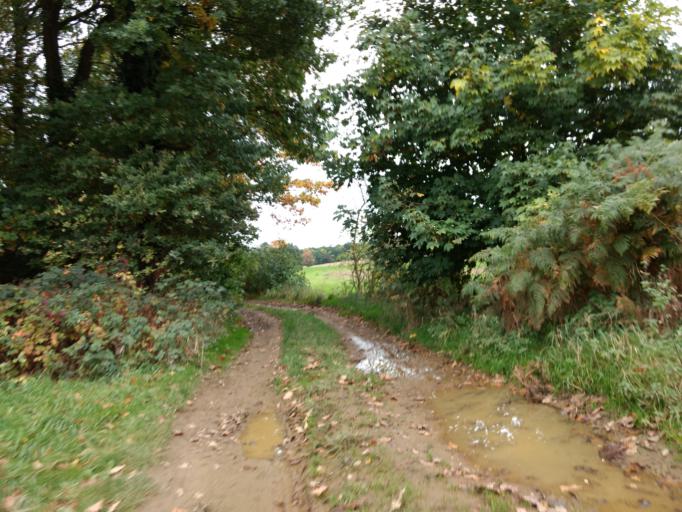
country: BE
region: Flanders
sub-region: Provincie Vlaams-Brabant
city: Diest
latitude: 50.9628
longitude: 5.0186
